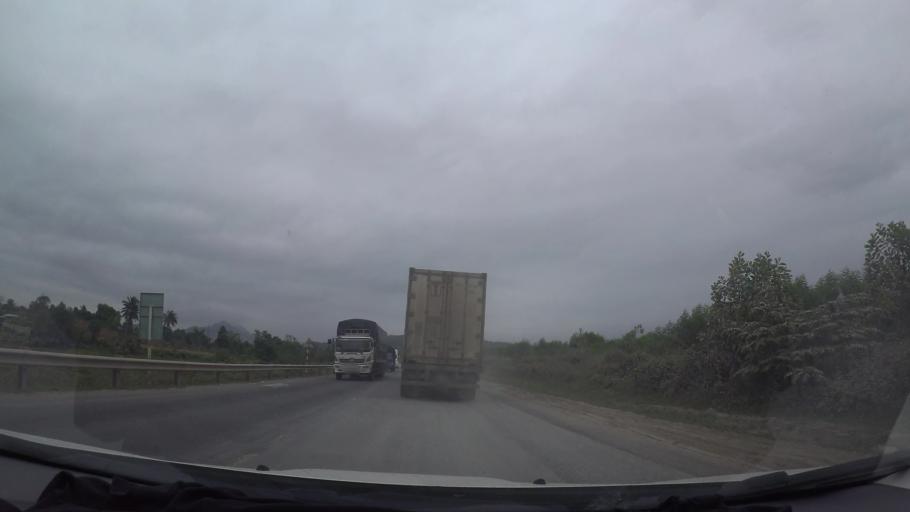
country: VN
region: Da Nang
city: Lien Chieu
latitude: 16.0899
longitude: 108.0854
